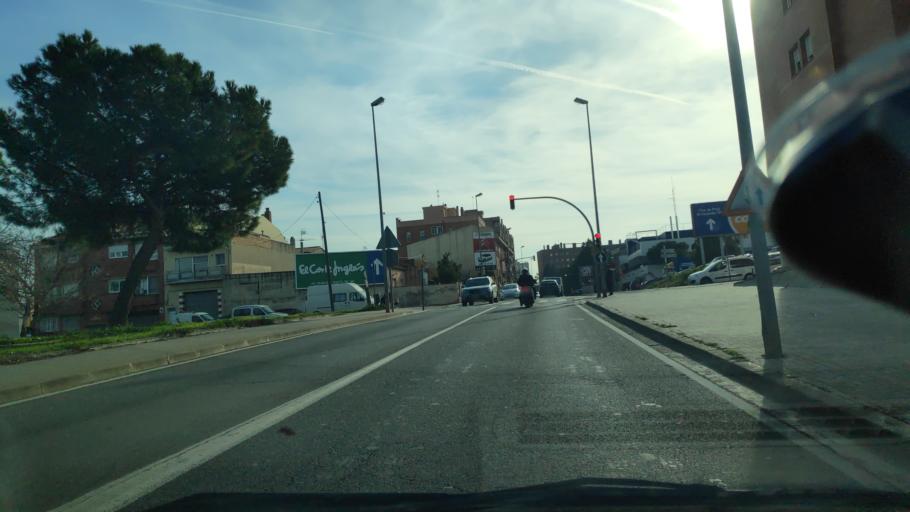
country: ES
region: Catalonia
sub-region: Provincia de Barcelona
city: Sabadell
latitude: 41.5650
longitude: 2.1010
